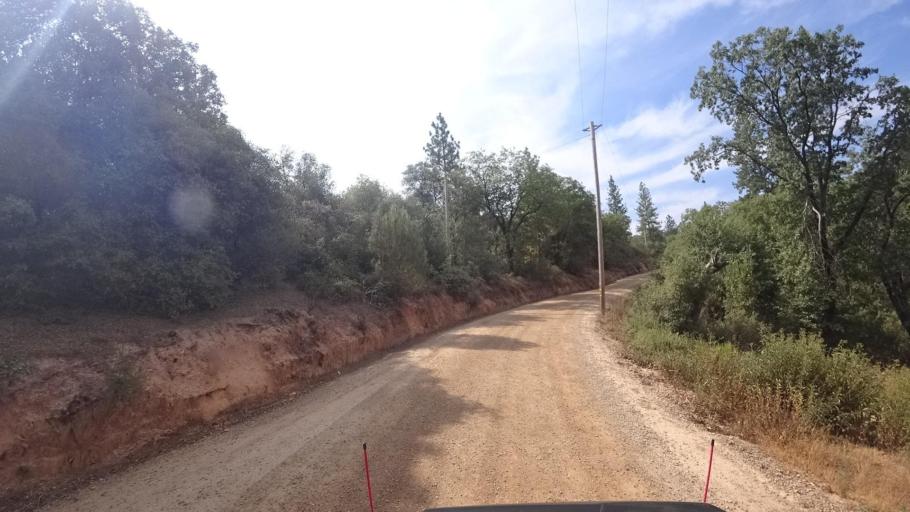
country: US
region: California
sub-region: Mariposa County
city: Midpines
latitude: 37.5687
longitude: -119.9964
